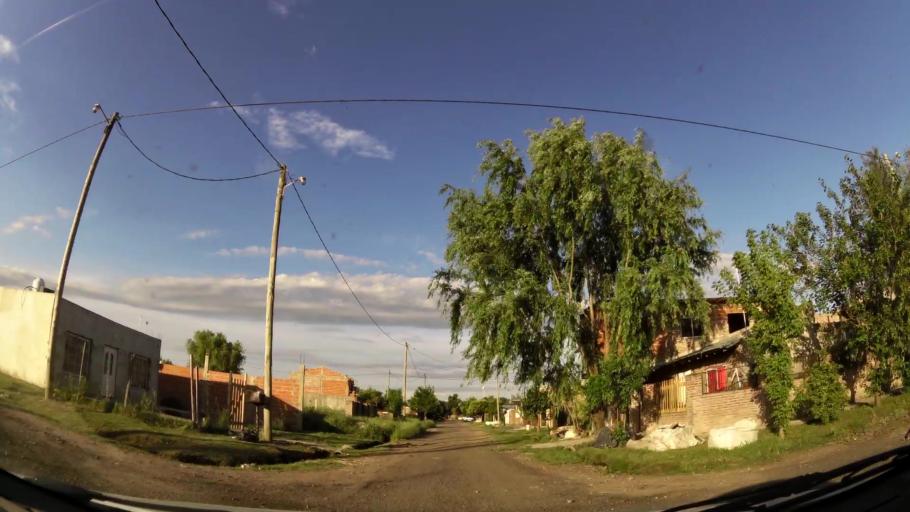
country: AR
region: Buenos Aires
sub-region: Partido de Merlo
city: Merlo
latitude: -34.7002
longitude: -58.7532
